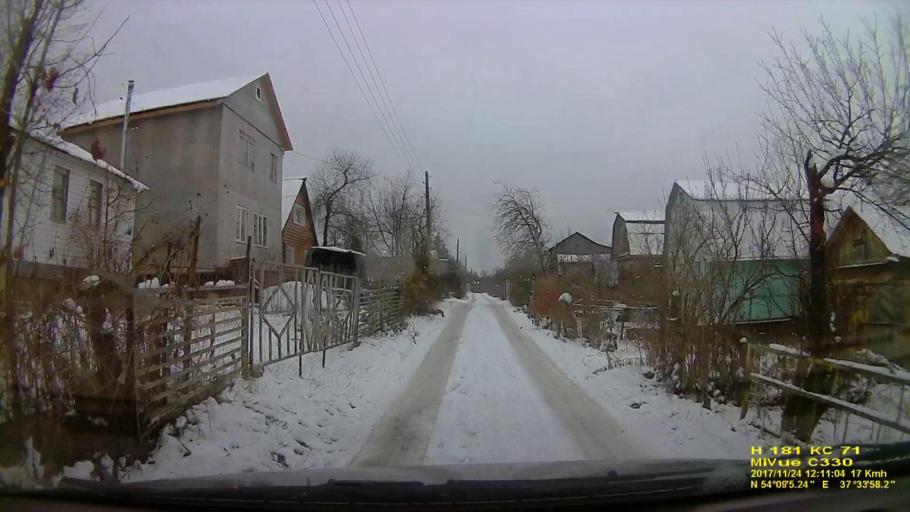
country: RU
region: Tula
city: Mendeleyevskiy
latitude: 54.1519
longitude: 37.5668
